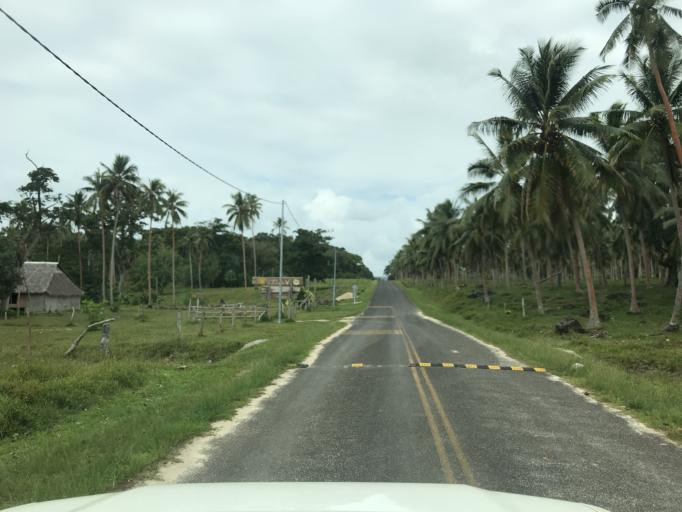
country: VU
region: Sanma
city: Port-Olry
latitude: -15.0466
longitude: 167.0719
